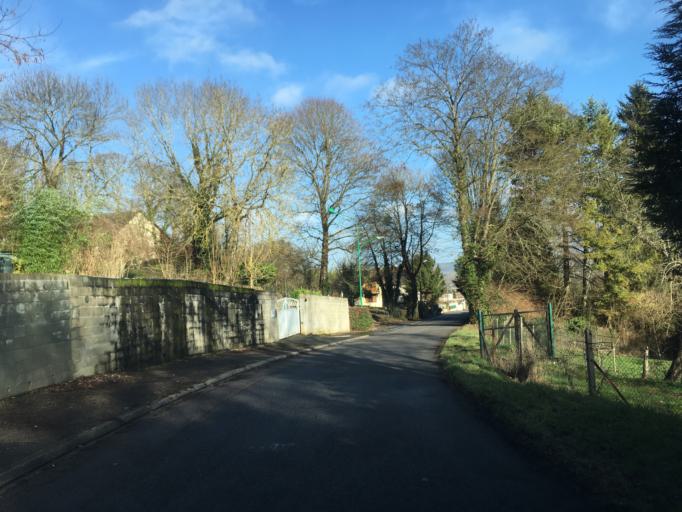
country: FR
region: Haute-Normandie
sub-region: Departement de l'Eure
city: Saint-Just
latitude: 49.1075
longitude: 1.4351
